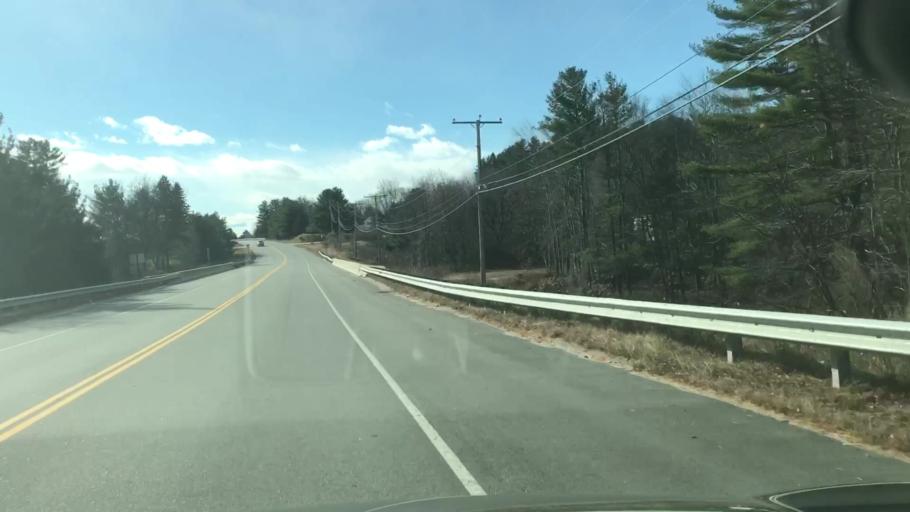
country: US
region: New Hampshire
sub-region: Merrimack County
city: Chichester
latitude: 43.2385
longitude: -71.4617
